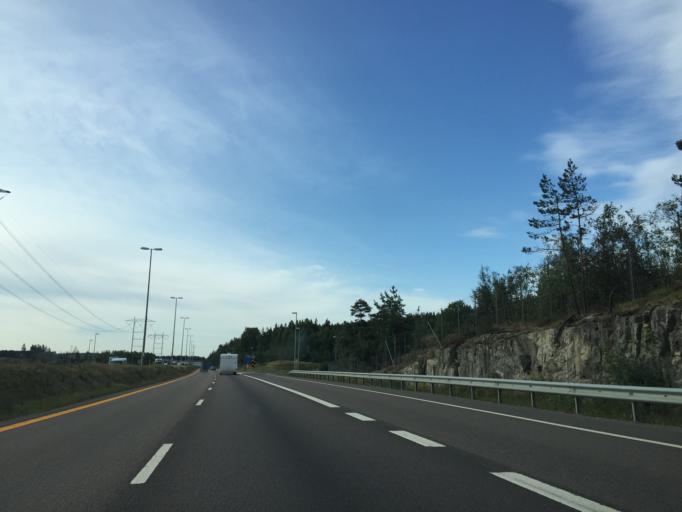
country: NO
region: Akershus
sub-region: Oppegard
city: Kolbotn
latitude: 59.7873
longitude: 10.8391
